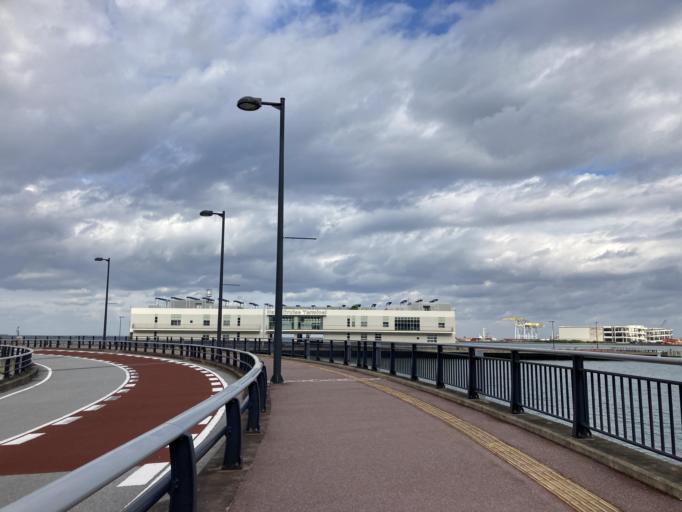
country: JP
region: Okinawa
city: Naha-shi
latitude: 26.2245
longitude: 127.6762
